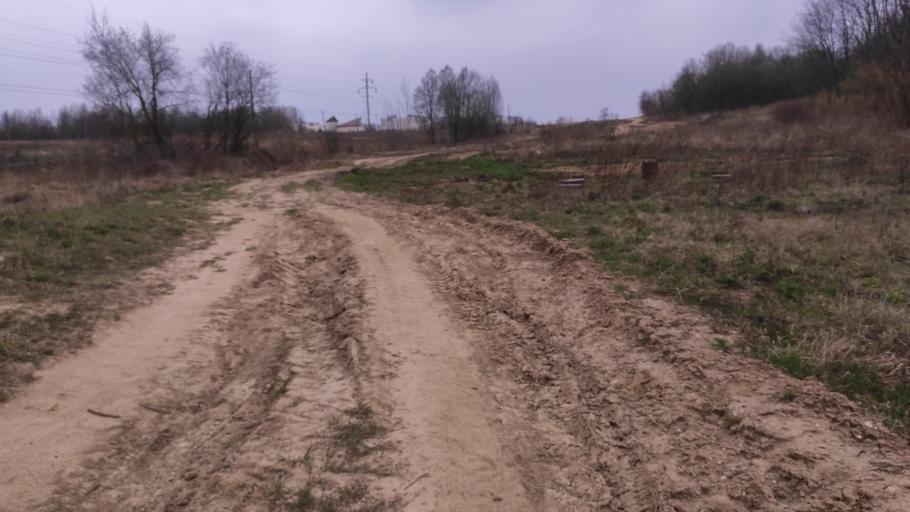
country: BY
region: Minsk
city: Novoye Medvezhino
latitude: 53.8872
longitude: 27.4646
